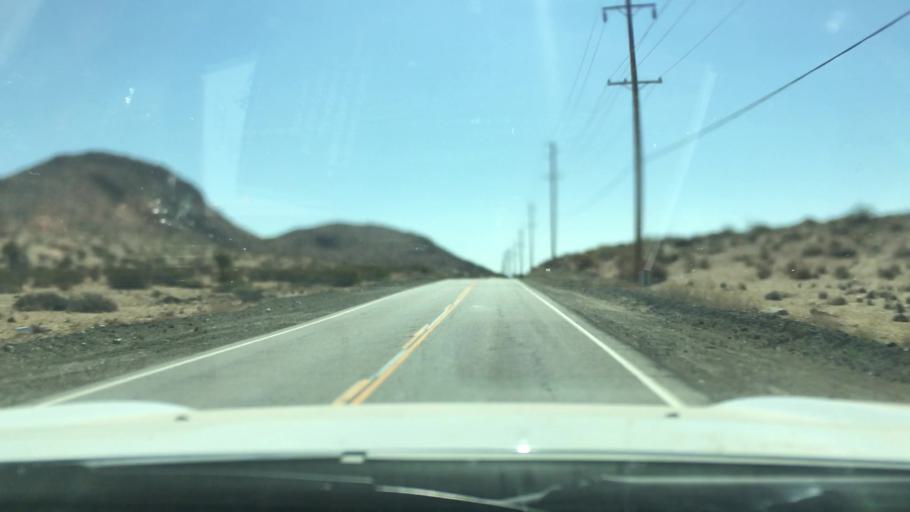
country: US
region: California
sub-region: Los Angeles County
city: Lake Los Angeles
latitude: 34.5798
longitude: -117.7389
